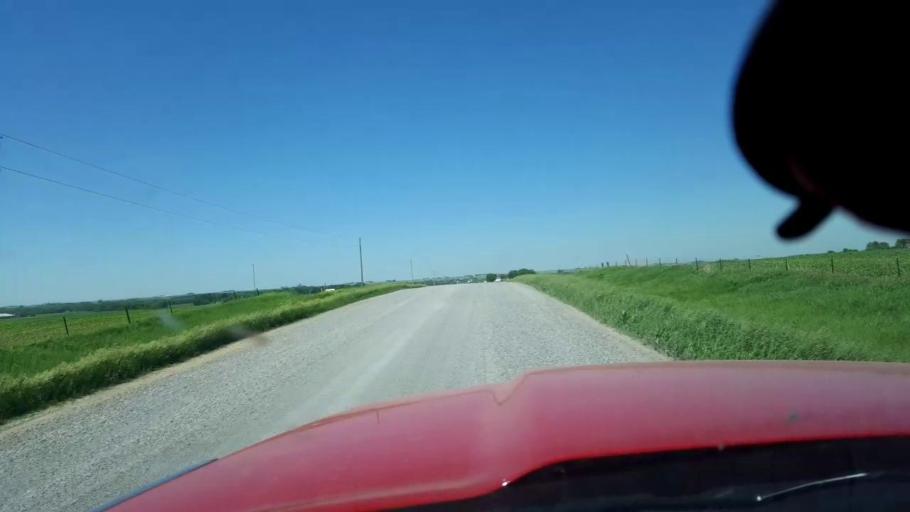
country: US
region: Iowa
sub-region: Chickasaw County
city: New Hampton
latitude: 43.2135
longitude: -92.2416
